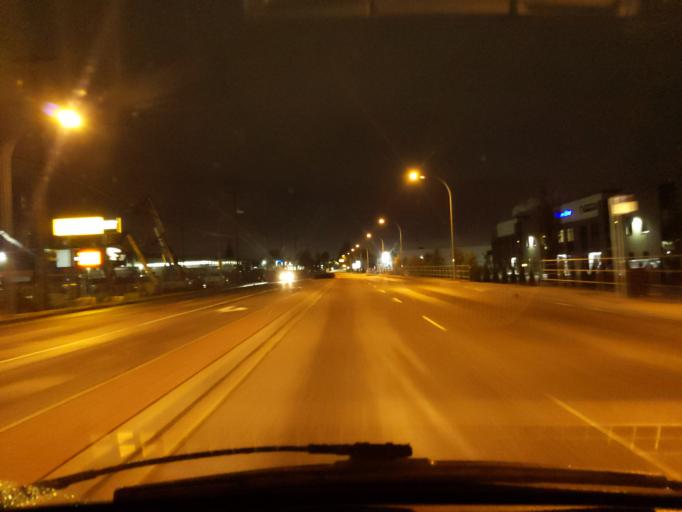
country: CA
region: British Columbia
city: Walnut Grove
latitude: 49.1768
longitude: -122.6745
